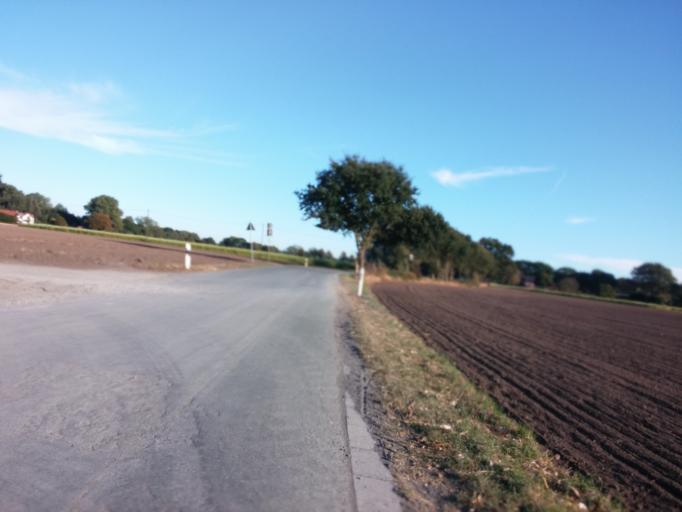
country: DE
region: North Rhine-Westphalia
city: Dorsten
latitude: 51.6419
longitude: 7.0110
